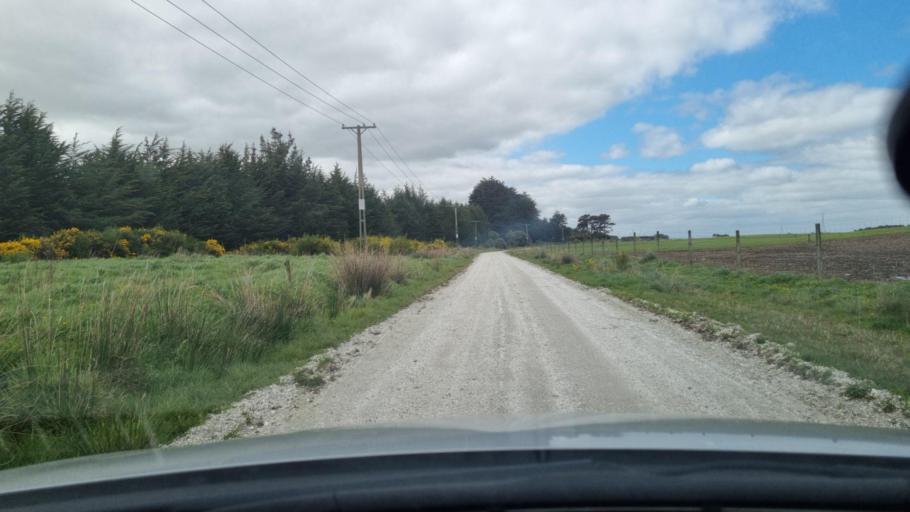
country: NZ
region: Southland
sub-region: Invercargill City
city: Invercargill
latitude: -46.4432
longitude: 168.4211
